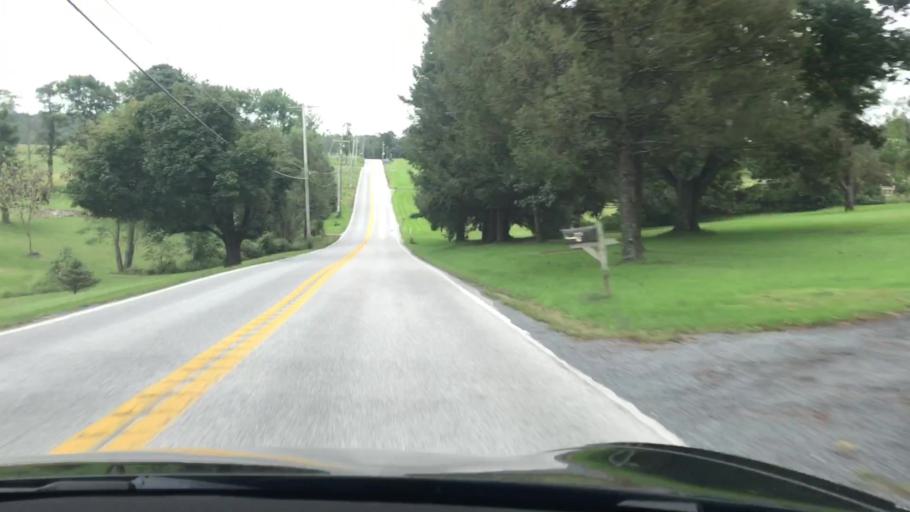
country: US
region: Pennsylvania
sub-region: York County
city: Dillsburg
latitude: 40.1180
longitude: -76.9577
